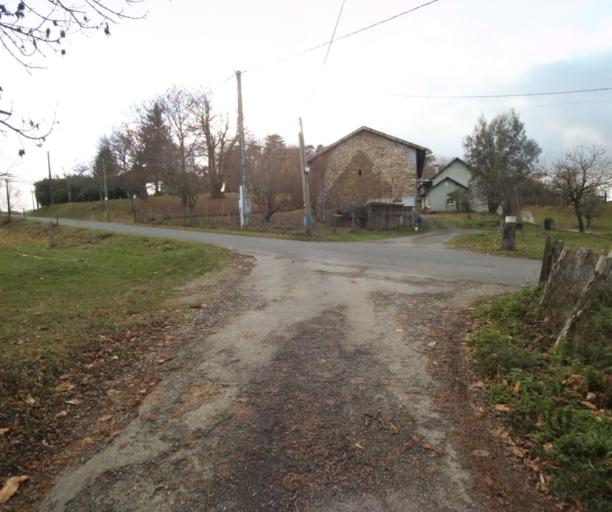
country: FR
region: Limousin
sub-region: Departement de la Correze
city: Laguenne
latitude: 45.2215
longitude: 1.7921
